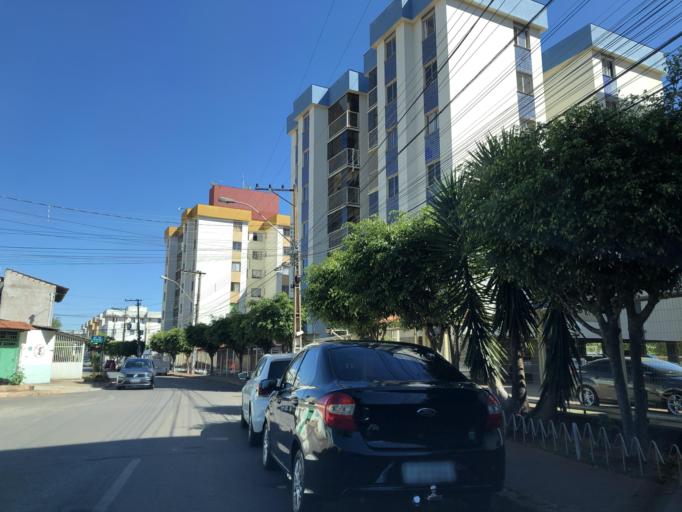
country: BR
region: Federal District
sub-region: Brasilia
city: Brasilia
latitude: -15.8672
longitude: -48.0630
